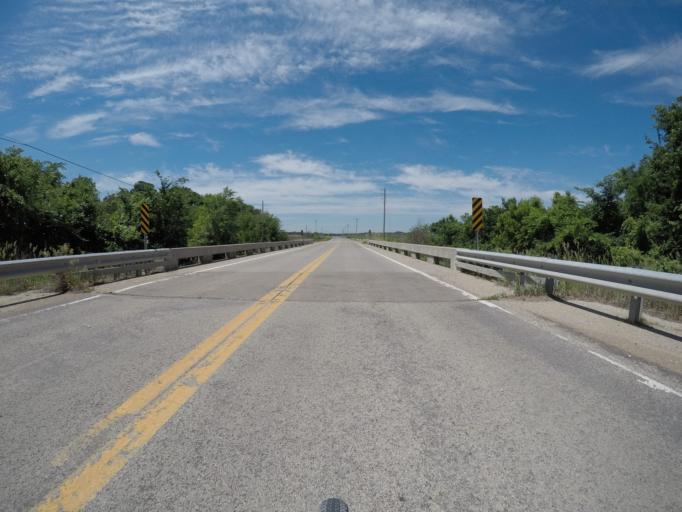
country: US
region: Kansas
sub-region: Wabaunsee County
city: Alma
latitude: 39.0461
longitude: -96.2515
